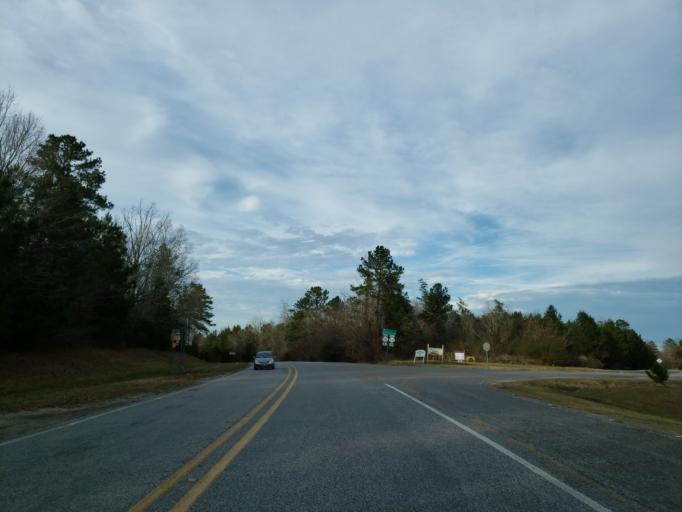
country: US
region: Mississippi
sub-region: Wayne County
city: Waynesboro
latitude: 31.8437
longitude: -88.6866
